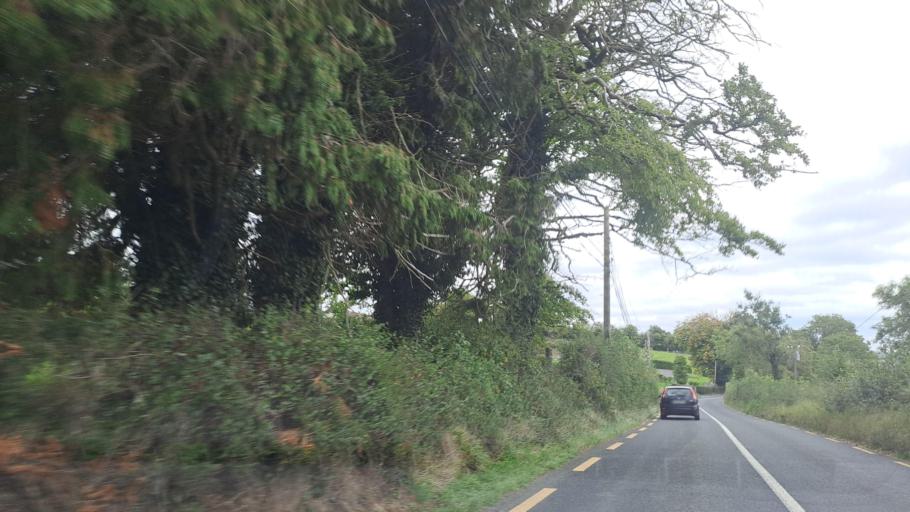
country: IE
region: Ulster
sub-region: An Cabhan
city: Bailieborough
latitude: 53.9888
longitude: -6.9079
